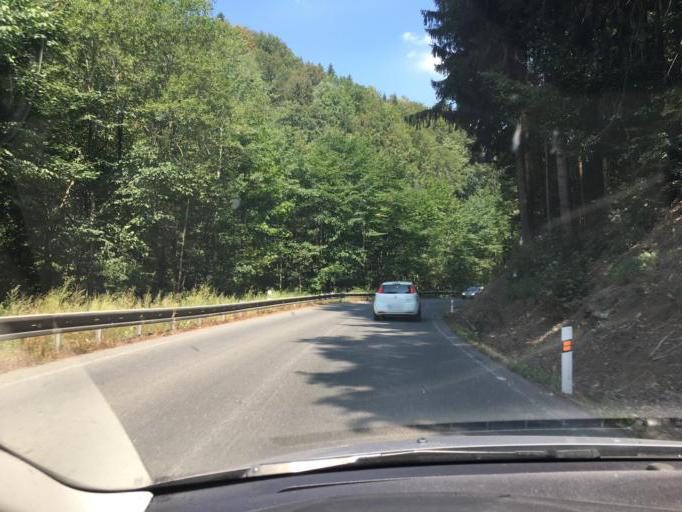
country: CZ
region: Liberecky
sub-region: Okres Semily
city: Ponikla
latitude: 50.6394
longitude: 15.4602
